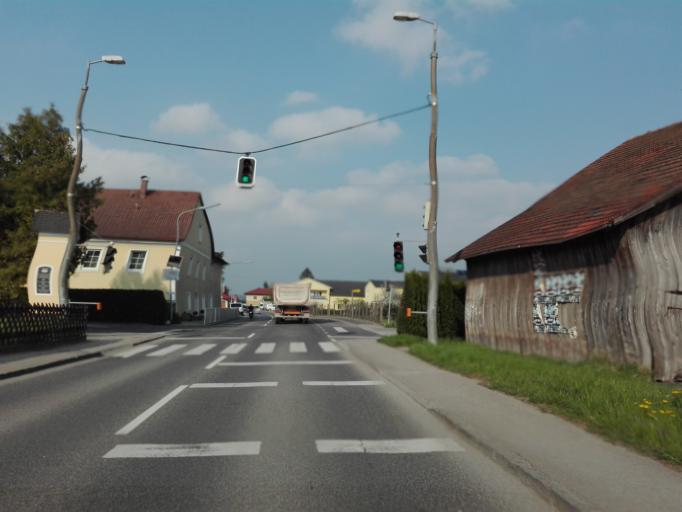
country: AT
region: Lower Austria
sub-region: Politischer Bezirk Amstetten
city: Ennsdorf
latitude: 48.2135
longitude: 14.4908
